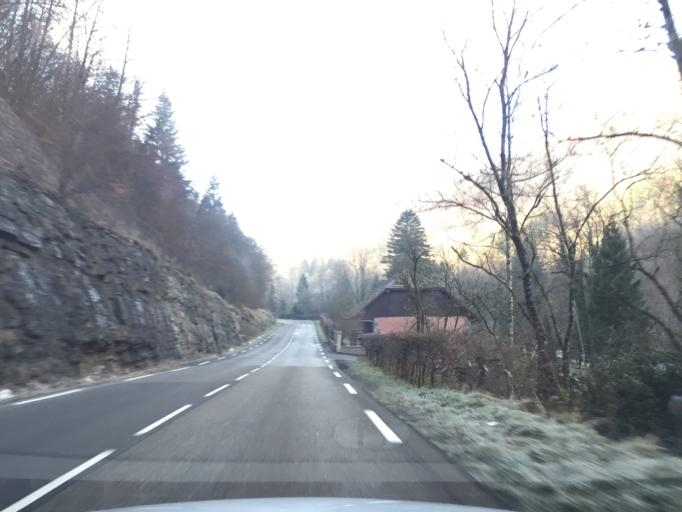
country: FR
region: Rhone-Alpes
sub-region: Departement de la Haute-Savoie
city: Gruffy
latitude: 45.7308
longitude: 6.0962
